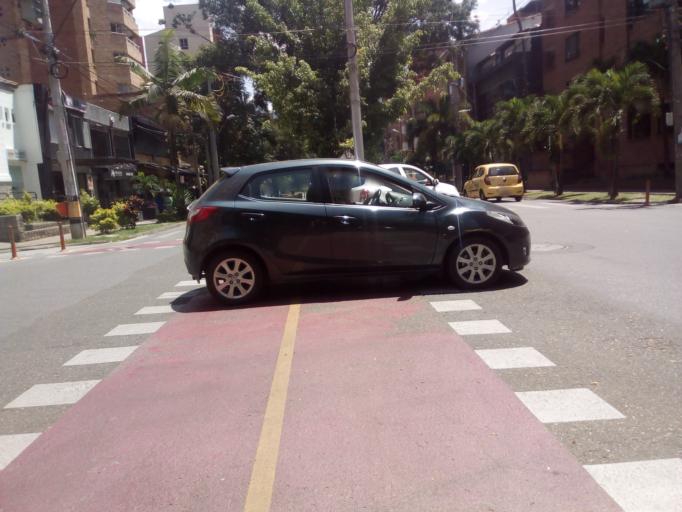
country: CO
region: Antioquia
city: Medellin
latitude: 6.2430
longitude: -75.5970
